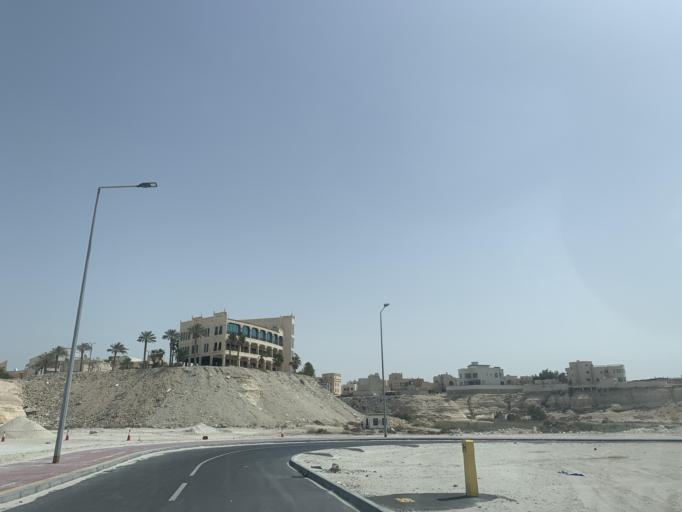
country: BH
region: Northern
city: Ar Rifa'
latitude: 26.1482
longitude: 50.5662
